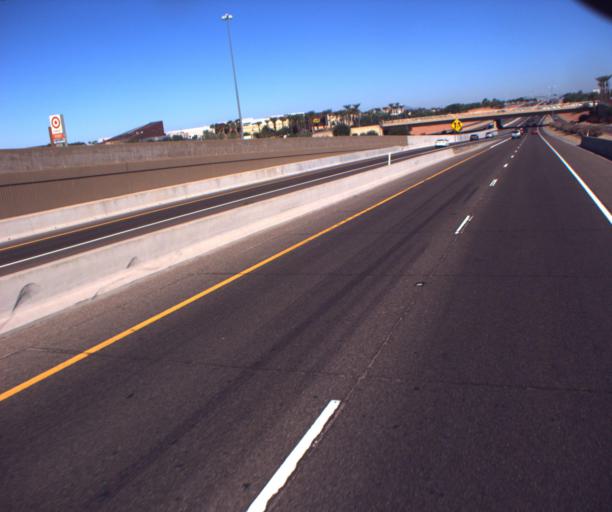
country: US
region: Arizona
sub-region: Maricopa County
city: Chandler
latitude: 33.2955
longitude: -111.8938
